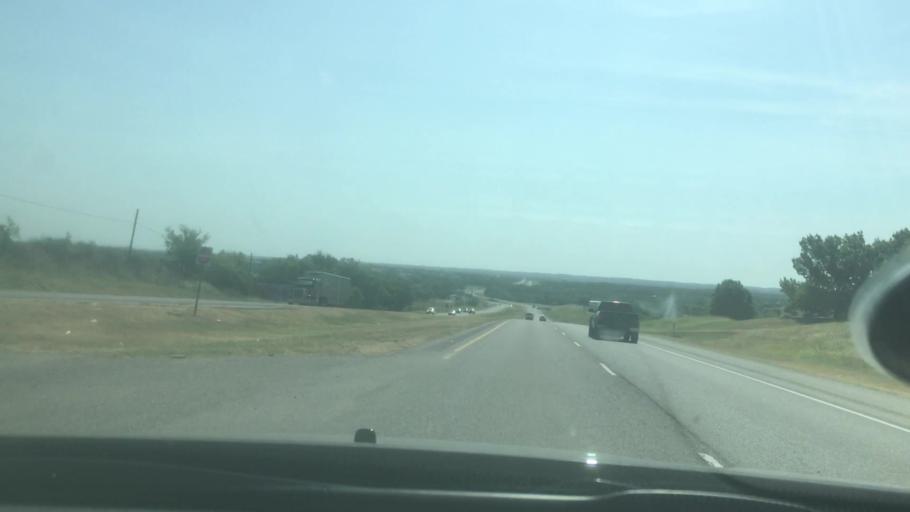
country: US
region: Oklahoma
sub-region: Murray County
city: Davis
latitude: 34.5060
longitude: -97.0463
